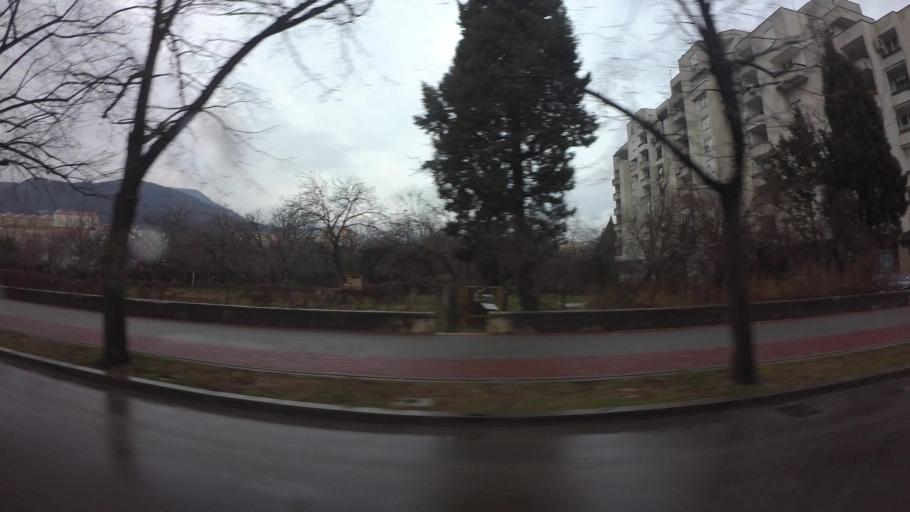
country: BA
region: Federation of Bosnia and Herzegovina
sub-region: Hercegovacko-Bosanski Kanton
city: Mostar
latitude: 43.3438
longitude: 17.8036
